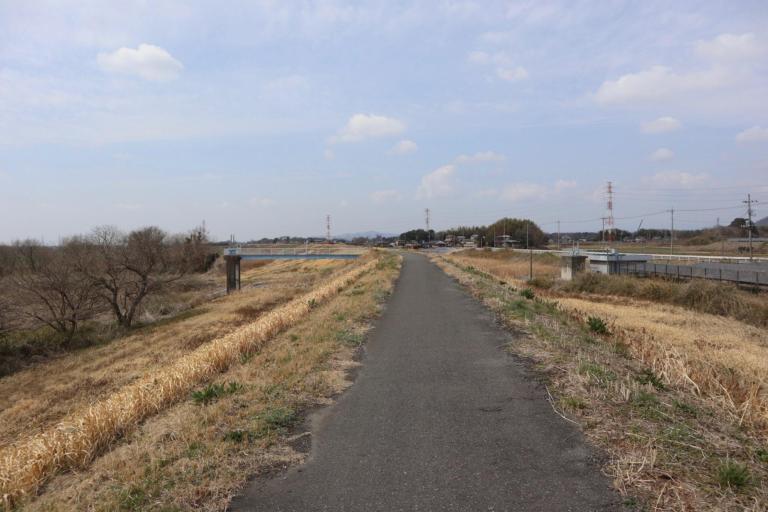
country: JP
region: Tochigi
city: Fujioka
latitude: 36.2725
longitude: 139.6327
